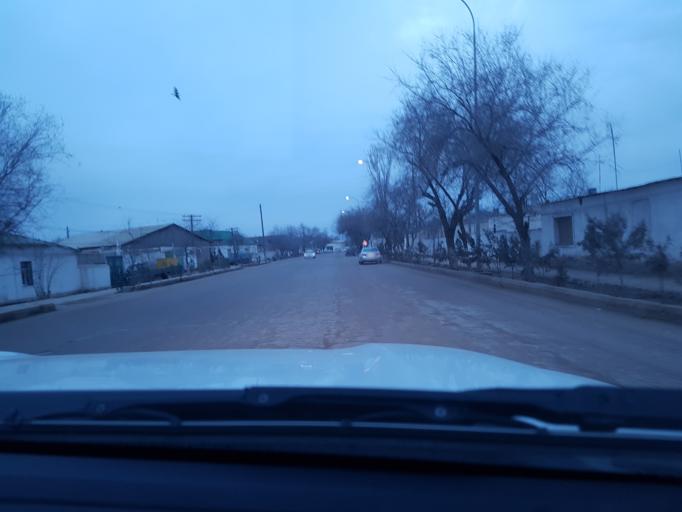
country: TM
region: Dasoguz
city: Yylanly
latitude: 41.8773
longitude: 59.6370
